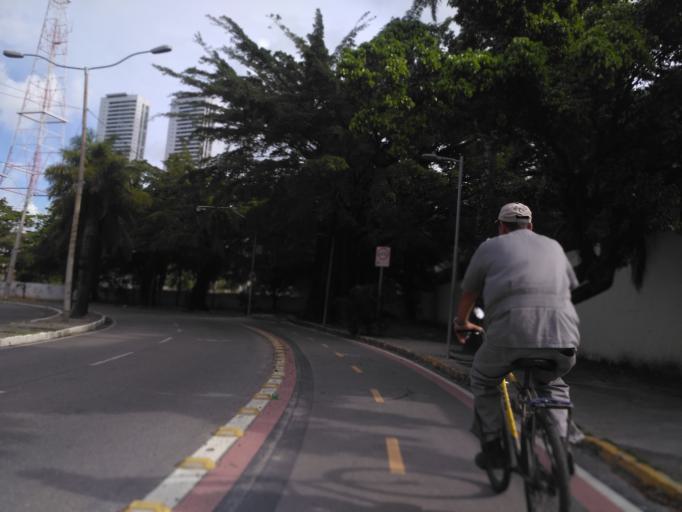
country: BR
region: Pernambuco
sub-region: Recife
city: Recife
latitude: -8.0473
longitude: -34.8751
